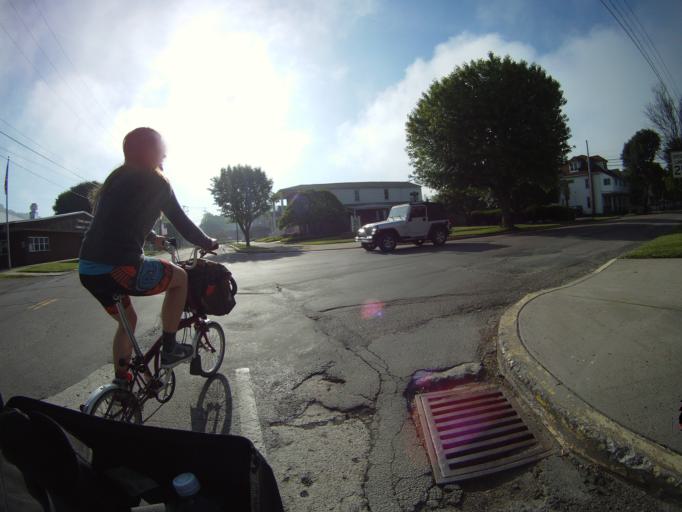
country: US
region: Pennsylvania
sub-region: Somerset County
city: Milford
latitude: 39.8118
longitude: -79.3581
